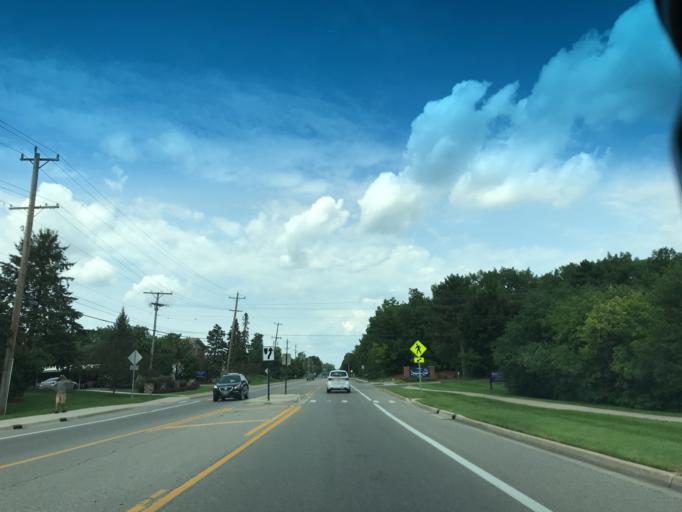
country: US
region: Michigan
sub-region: Washtenaw County
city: Ypsilanti
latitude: 42.2532
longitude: -83.6611
